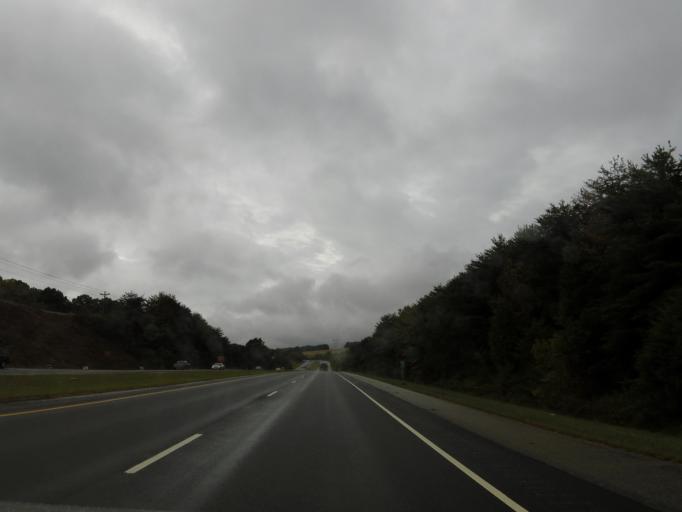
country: US
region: Tennessee
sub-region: Blount County
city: Louisville
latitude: 35.7579
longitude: -84.0566
